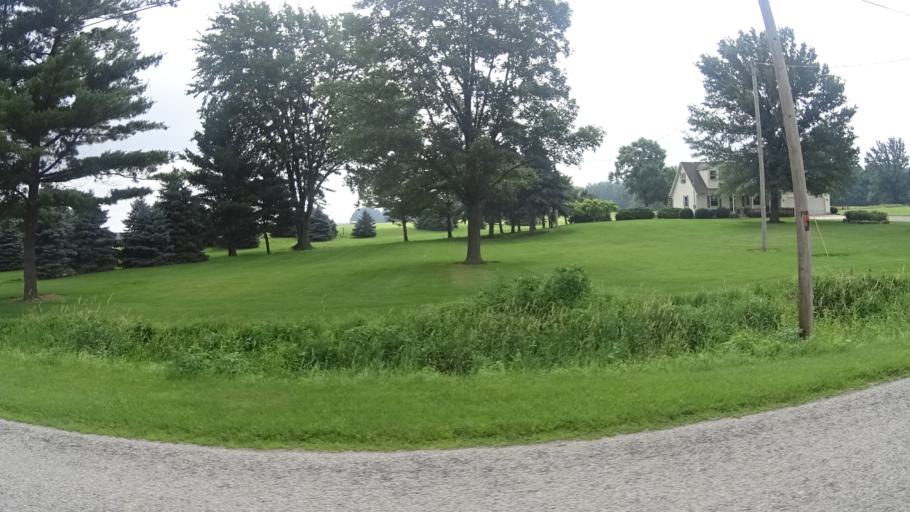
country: US
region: Ohio
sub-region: Huron County
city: Wakeman
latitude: 41.3005
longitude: -82.4811
